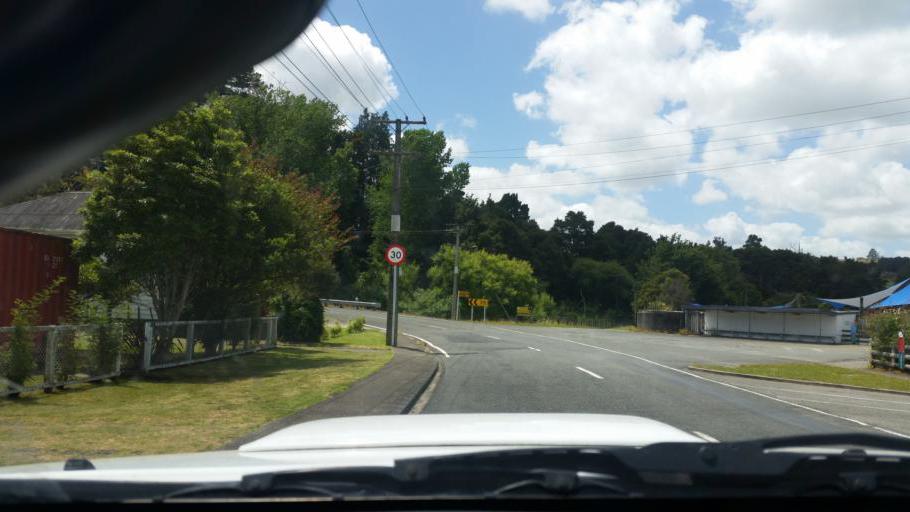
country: NZ
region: Northland
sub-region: Whangarei
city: Ruakaka
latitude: -36.0998
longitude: 174.2331
